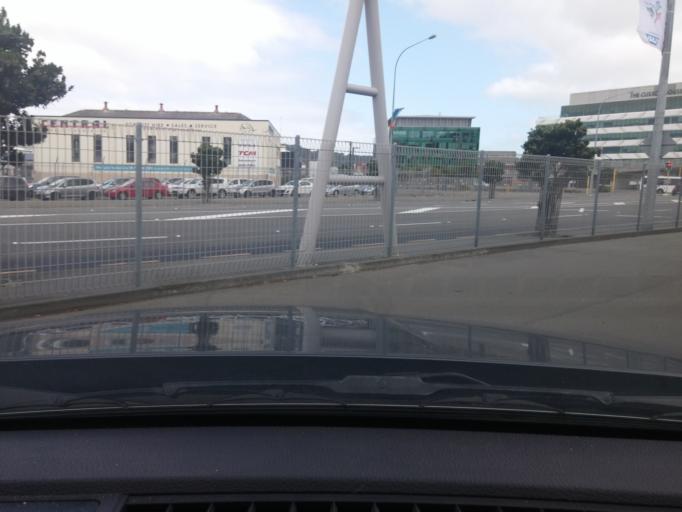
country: NZ
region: Wellington
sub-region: Wellington City
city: Wellington
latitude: -41.2760
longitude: 174.7845
